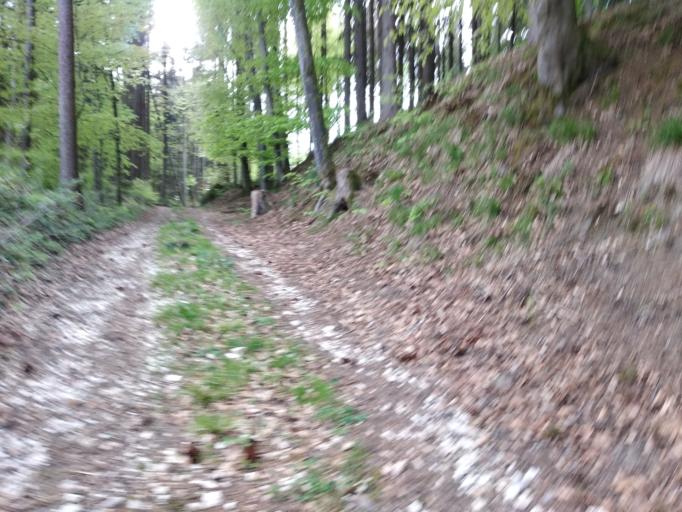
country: DE
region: Bavaria
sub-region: Swabia
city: Woringen
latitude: 47.9265
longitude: 10.1928
